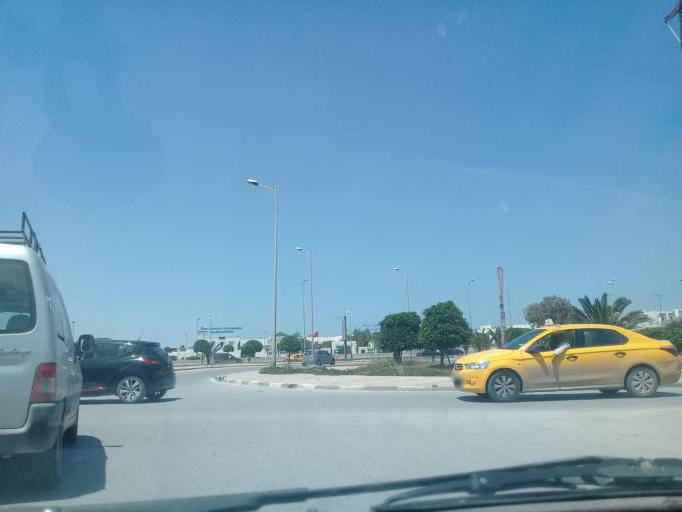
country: TN
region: Tunis
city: La Goulette
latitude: 36.8462
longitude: 10.2596
